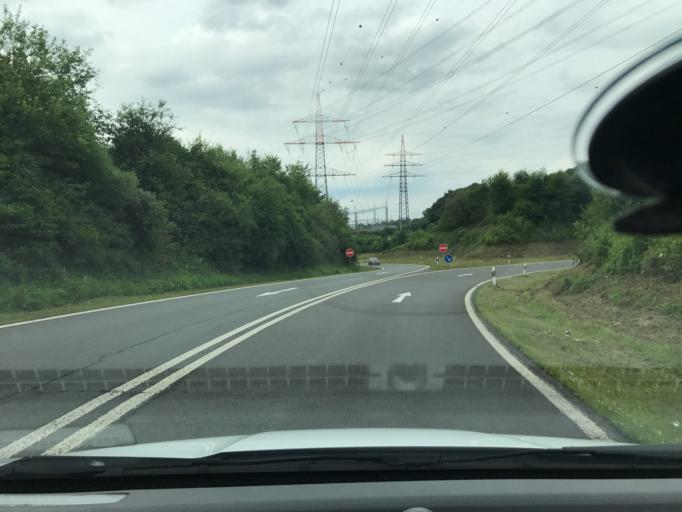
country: DE
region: North Rhine-Westphalia
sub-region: Regierungsbezirk Dusseldorf
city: Remscheid
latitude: 51.2275
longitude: 7.2313
